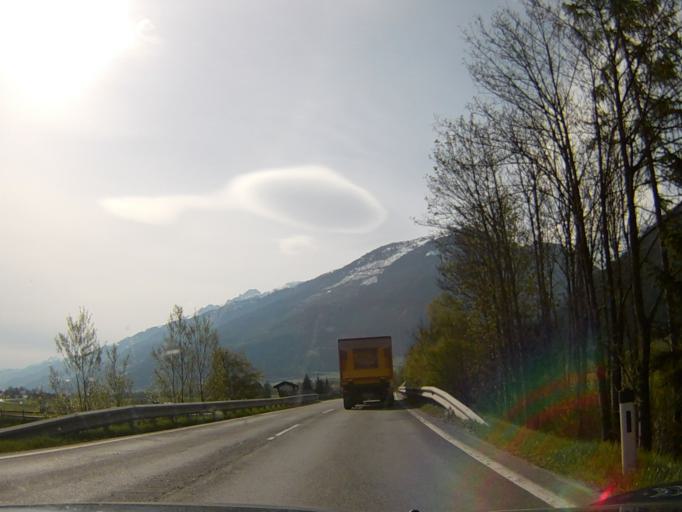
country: AT
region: Salzburg
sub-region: Politischer Bezirk Zell am See
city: Stuhlfelden
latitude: 47.2872
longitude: 12.5388
